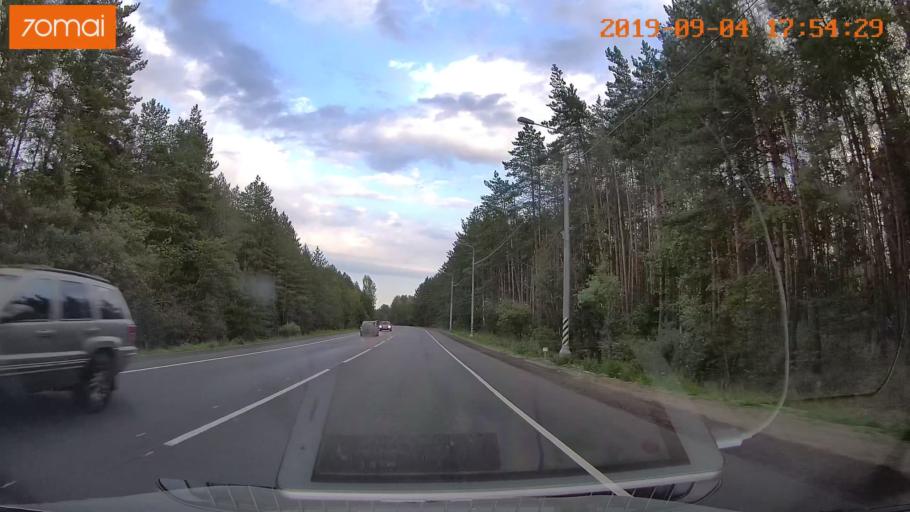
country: RU
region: Moskovskaya
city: Imeni Tsyurupy
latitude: 55.5101
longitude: 38.7464
